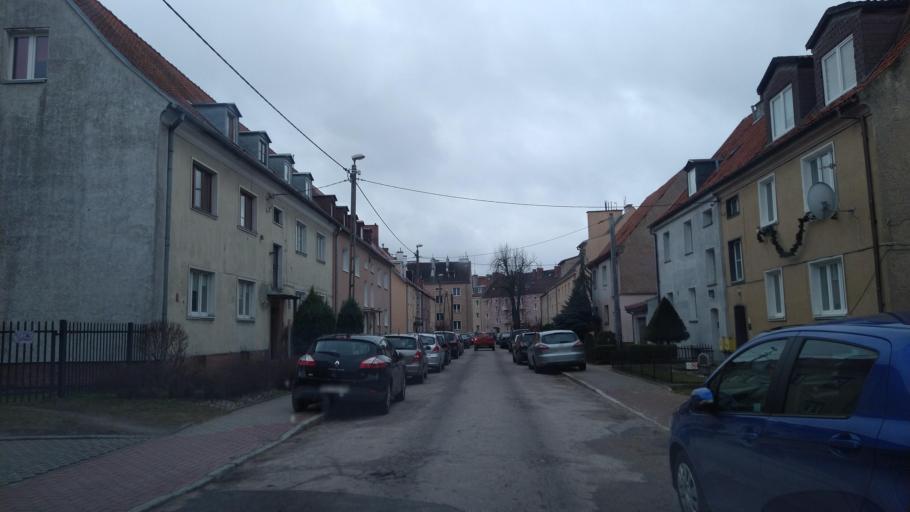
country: PL
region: Warmian-Masurian Voivodeship
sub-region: Powiat olsztynski
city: Olsztyn
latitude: 53.7892
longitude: 20.4931
